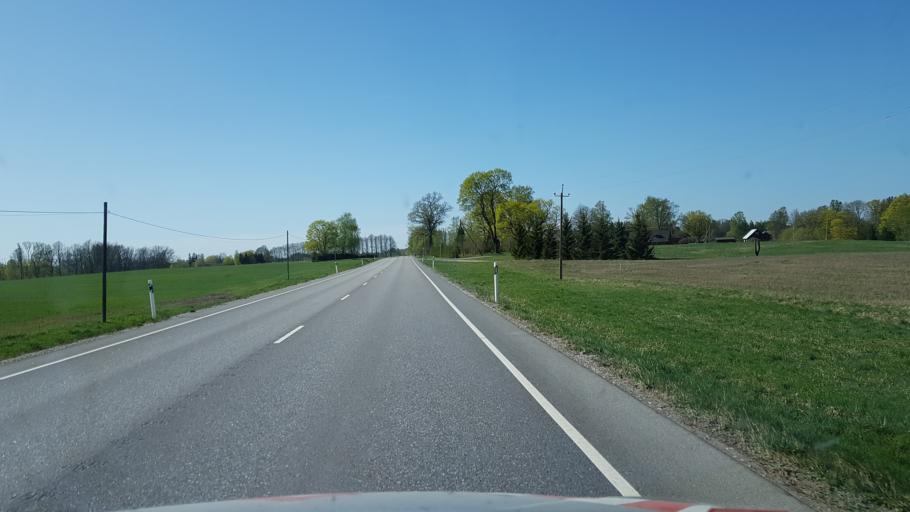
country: EE
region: Viljandimaa
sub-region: Karksi vald
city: Karksi-Nuia
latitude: 58.1121
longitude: 25.5071
